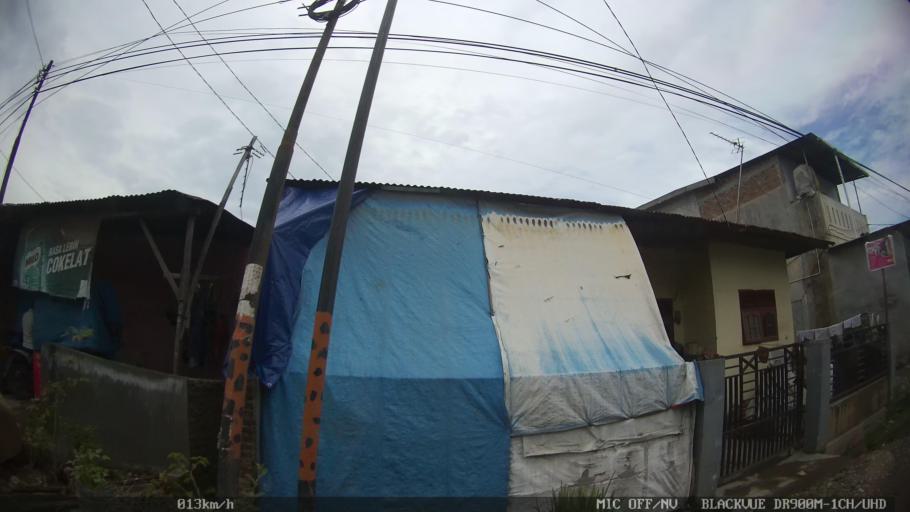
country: ID
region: North Sumatra
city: Sunggal
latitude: 3.6087
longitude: 98.6054
